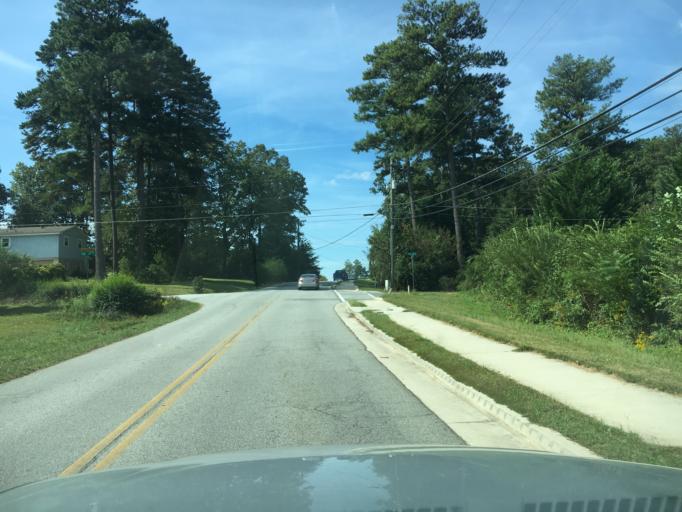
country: US
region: Georgia
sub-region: Gwinnett County
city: Duluth
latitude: 33.9715
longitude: -84.1418
